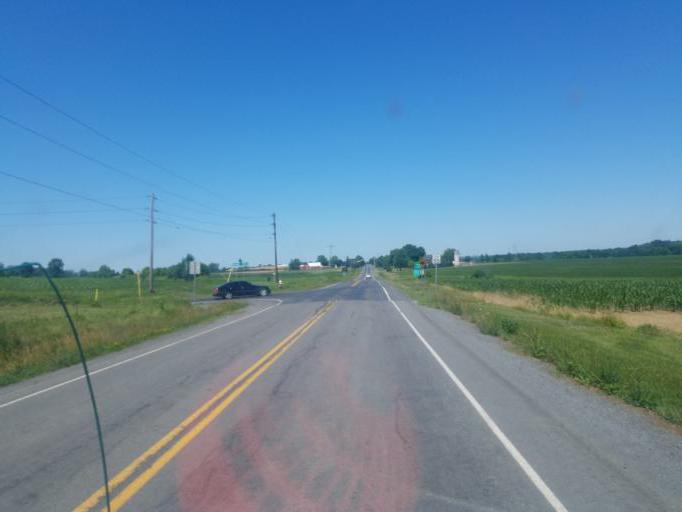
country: US
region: New York
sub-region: Yates County
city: Penn Yan
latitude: 42.7636
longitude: -77.0147
